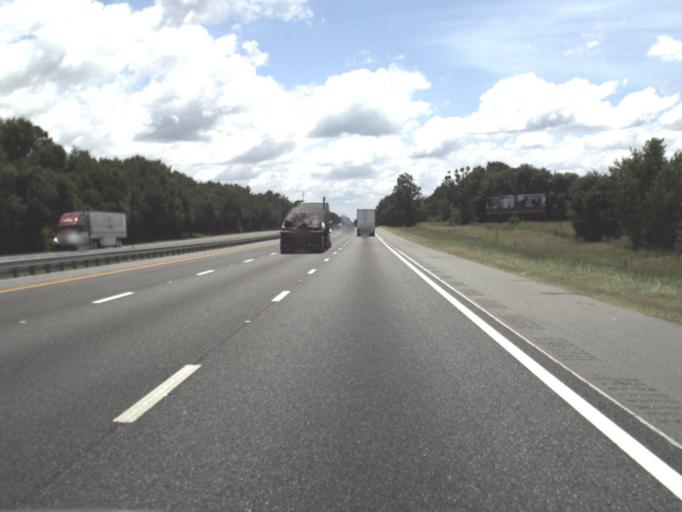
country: US
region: Florida
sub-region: Columbia County
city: Lake City
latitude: 30.0484
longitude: -82.6209
